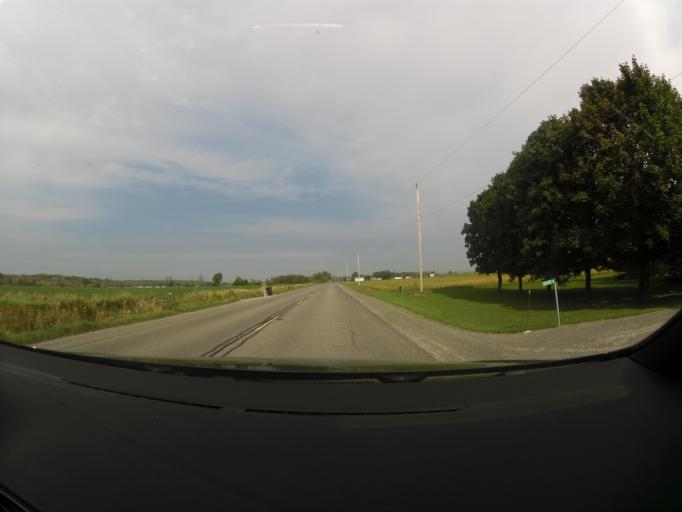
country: CA
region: Ontario
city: Bells Corners
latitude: 45.4040
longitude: -76.0242
